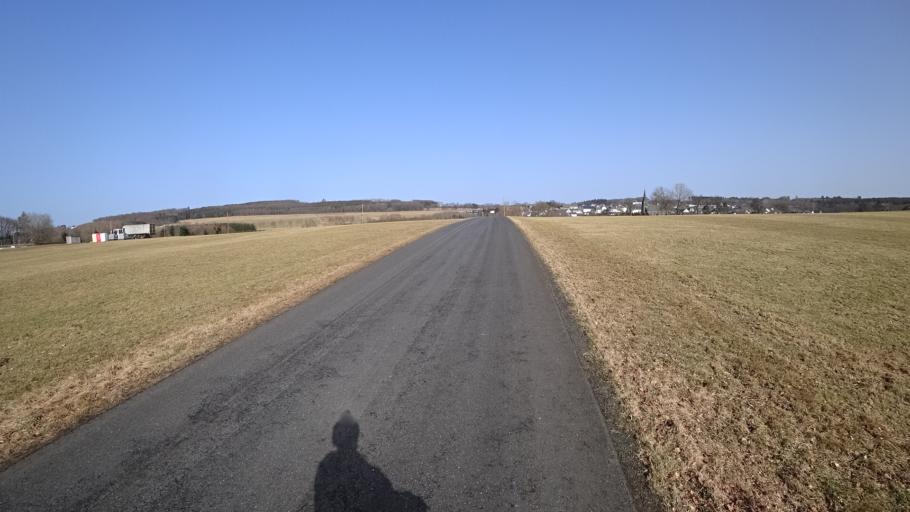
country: DE
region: Rheinland-Pfalz
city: Luckenbach
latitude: 50.7079
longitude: 7.8453
